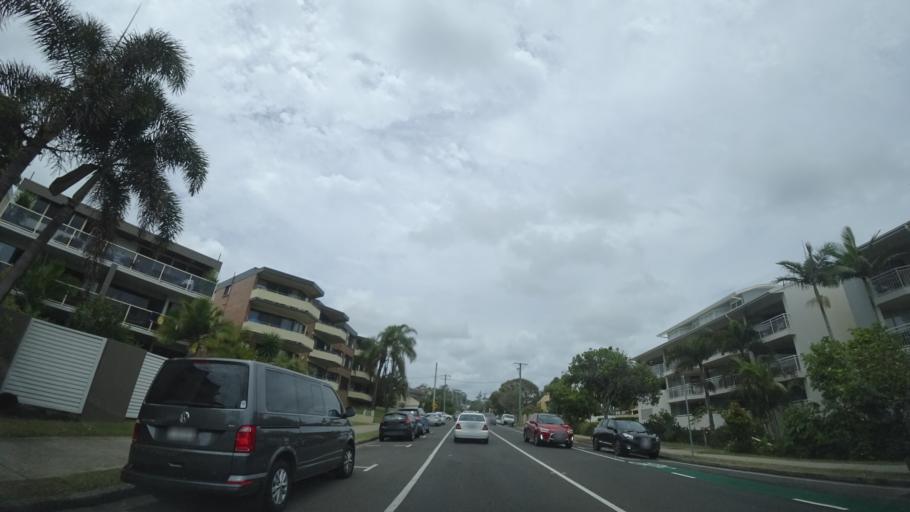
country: AU
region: Queensland
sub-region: Sunshine Coast
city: Mooloolaba
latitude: -26.6709
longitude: 153.1076
